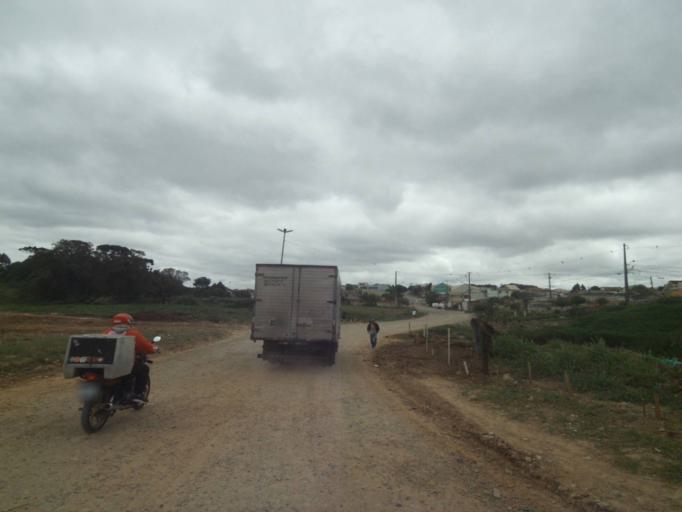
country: BR
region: Parana
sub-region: Sao Jose Dos Pinhais
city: Sao Jose dos Pinhais
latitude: -25.5542
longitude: -49.2665
